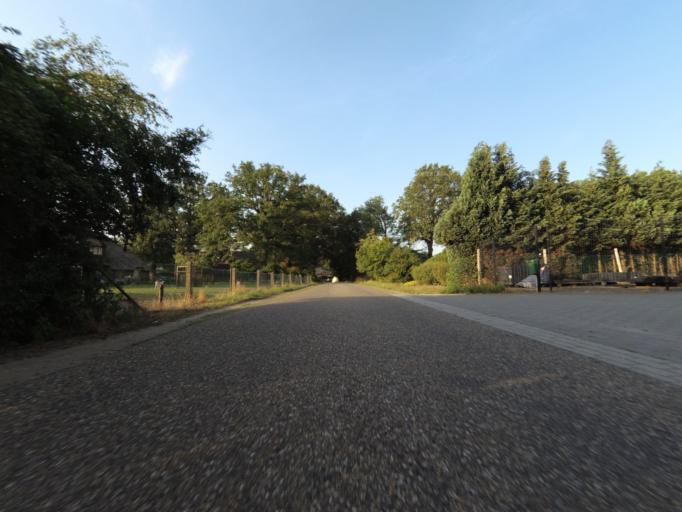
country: NL
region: Gelderland
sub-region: Gemeente Lochem
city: Laren
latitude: 52.2831
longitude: 6.4041
